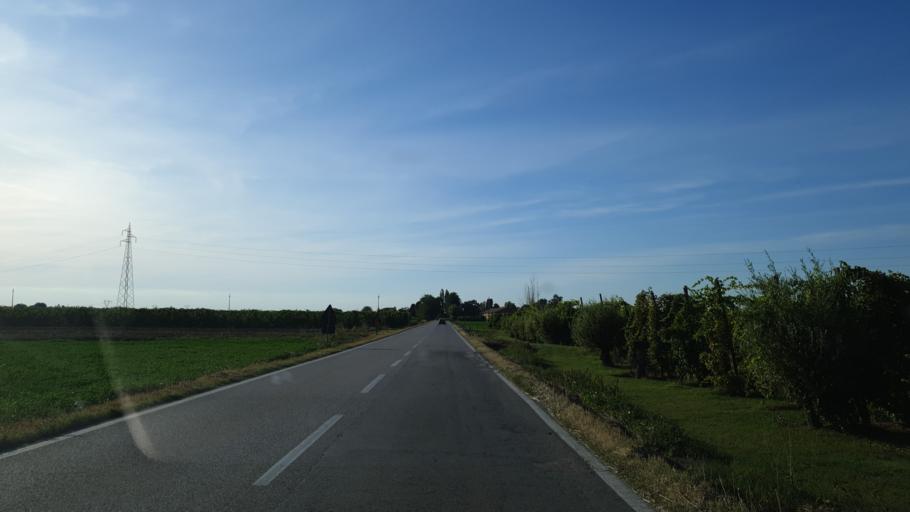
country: IT
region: Emilia-Romagna
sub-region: Provincia di Ravenna
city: Voltana
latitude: 44.5421
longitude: 11.9836
